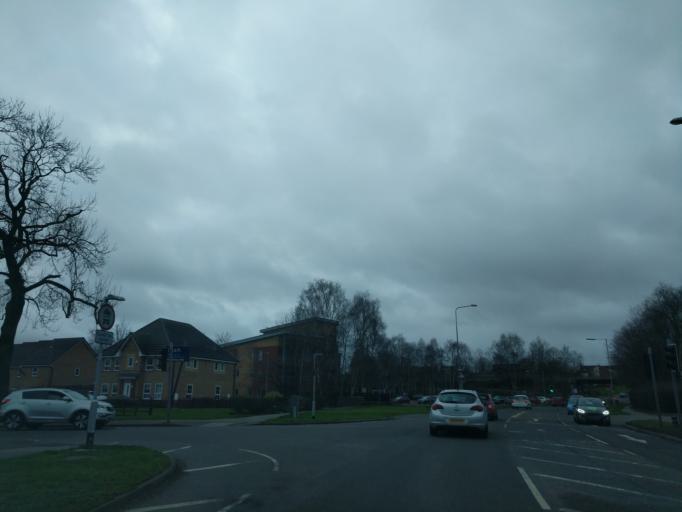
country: GB
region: England
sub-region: Staffordshire
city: Cannock
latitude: 52.6866
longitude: -2.0196
